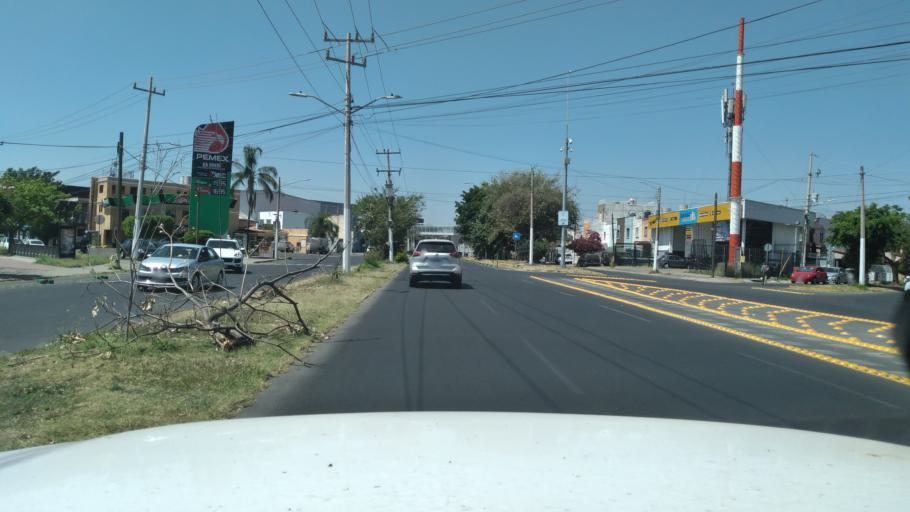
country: MX
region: Jalisco
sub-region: Zapopan
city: Zapopan
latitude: 20.7320
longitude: -103.3849
